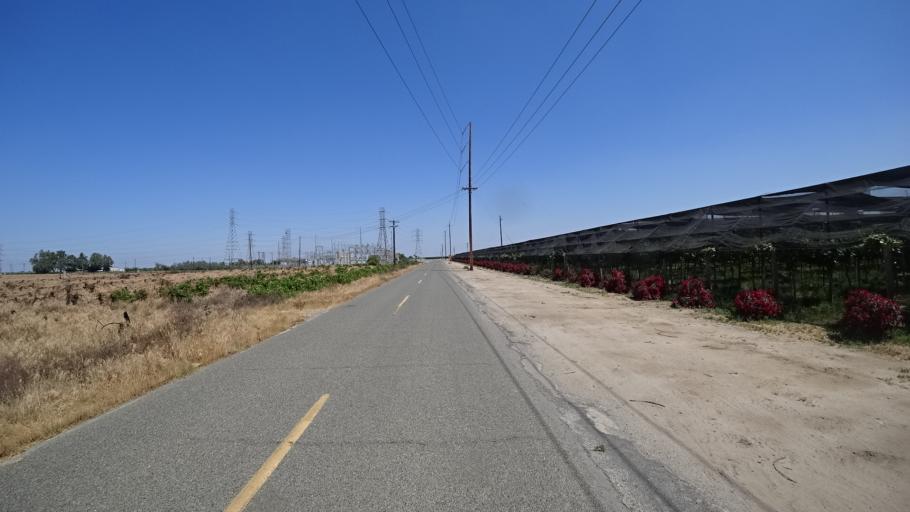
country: US
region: California
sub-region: Fresno County
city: Kingsburg
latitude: 36.4864
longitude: -119.5820
